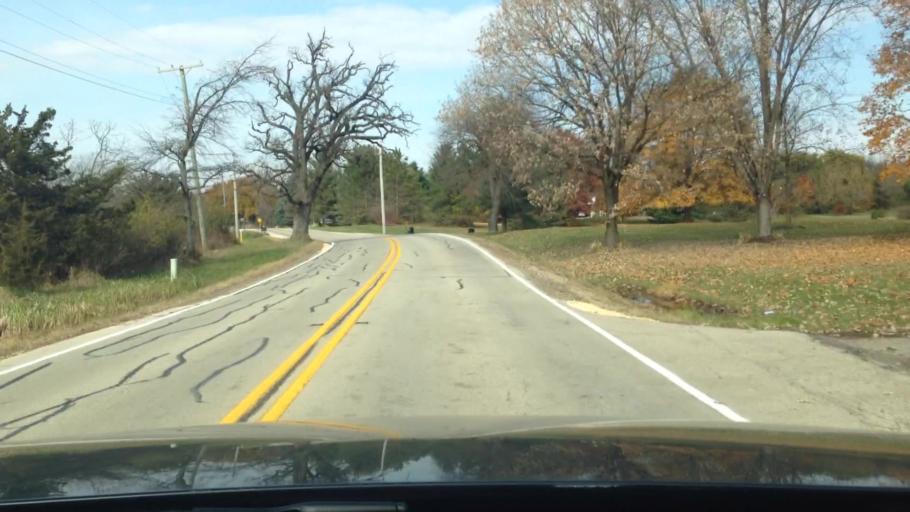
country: US
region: Illinois
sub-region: McHenry County
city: Woodstock
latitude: 42.2585
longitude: -88.4480
